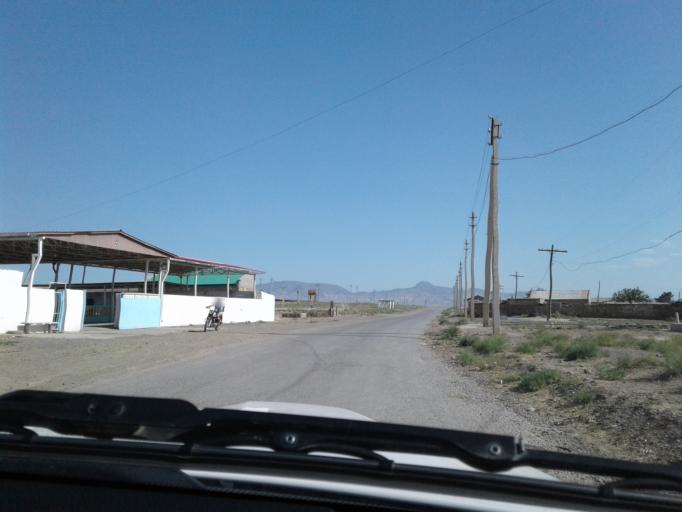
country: TM
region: Balkan
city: Serdar
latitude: 38.7112
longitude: 56.3400
